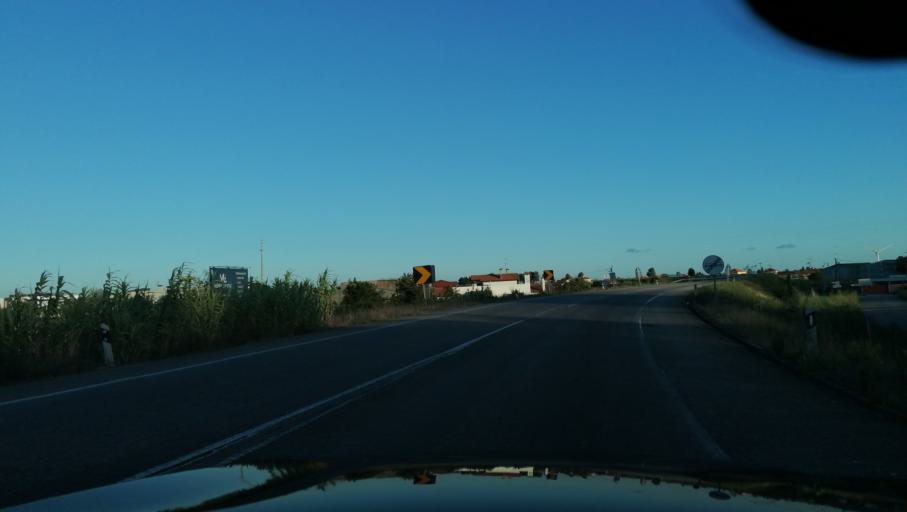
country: PT
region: Aveiro
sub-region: Aveiro
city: Oliveirinha
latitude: 40.5963
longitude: -8.6127
